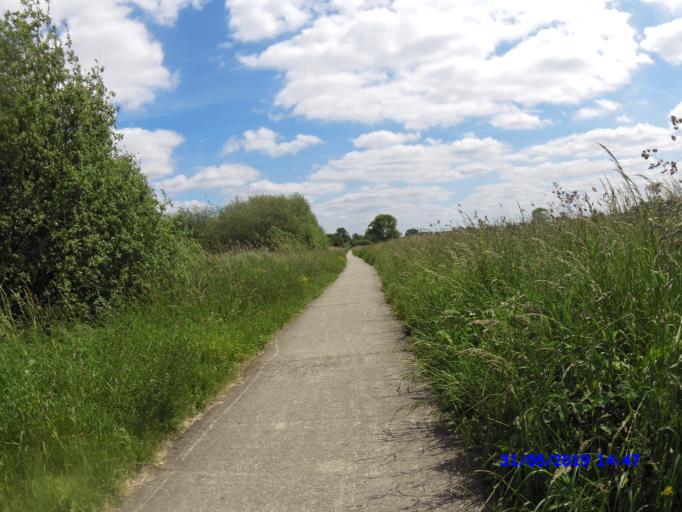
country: FR
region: Nord-Pas-de-Calais
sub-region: Departement du Nord
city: Deulemont
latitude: 50.7960
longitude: 2.9559
